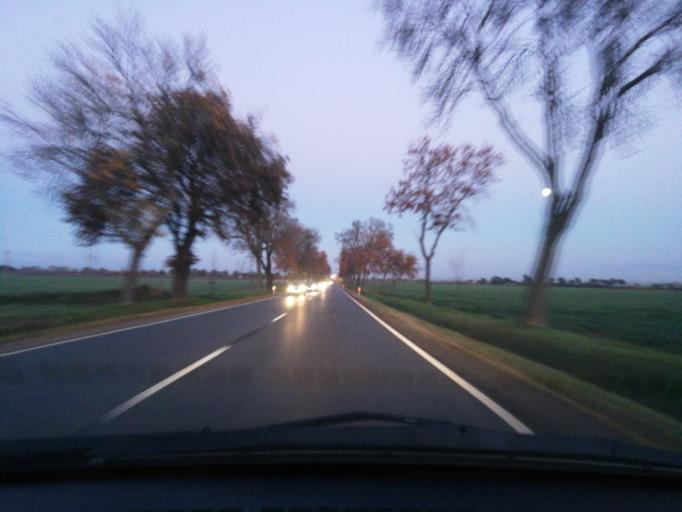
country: PL
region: Lodz Voivodeship
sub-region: Powiat brzezinski
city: Rogow
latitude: 51.8072
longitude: 19.8587
